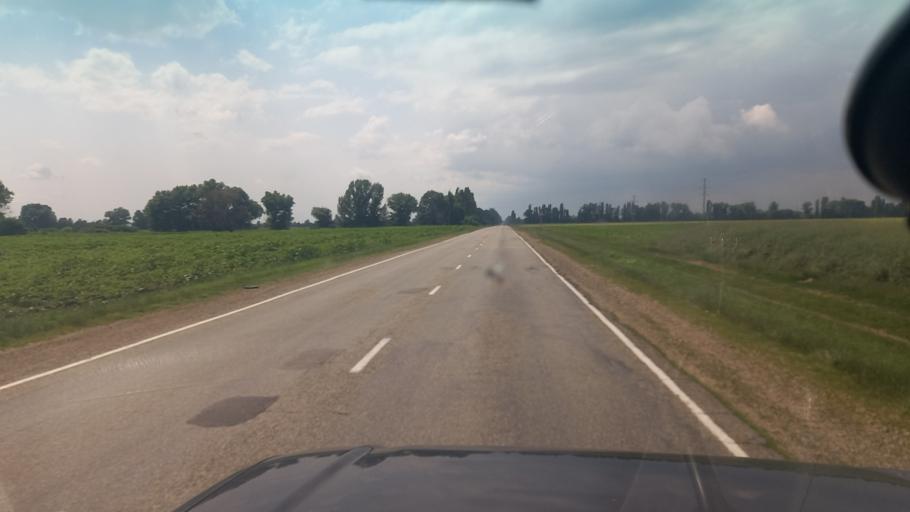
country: RU
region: Adygeya
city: Koshekhabl'
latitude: 44.9094
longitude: 40.4531
